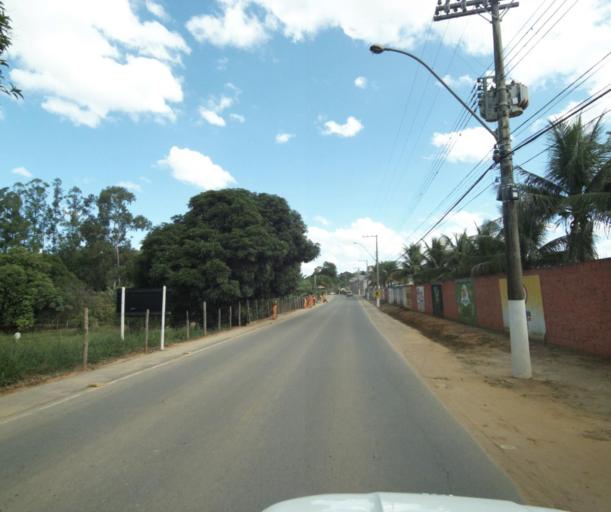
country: BR
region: Espirito Santo
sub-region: Sao Jose Do Calcado
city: Sao Jose do Calcado
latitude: -21.0347
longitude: -41.6521
